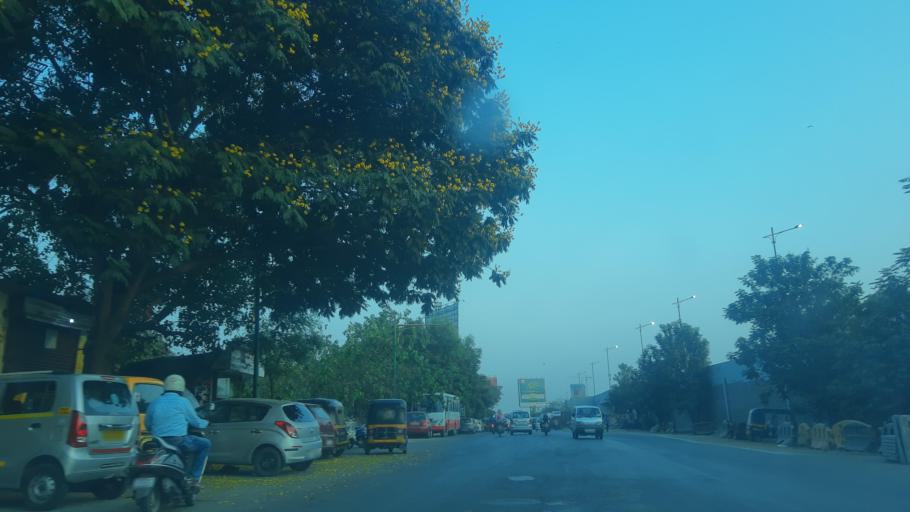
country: IN
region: Maharashtra
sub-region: Thane
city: Thane
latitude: 19.1836
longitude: 72.9656
